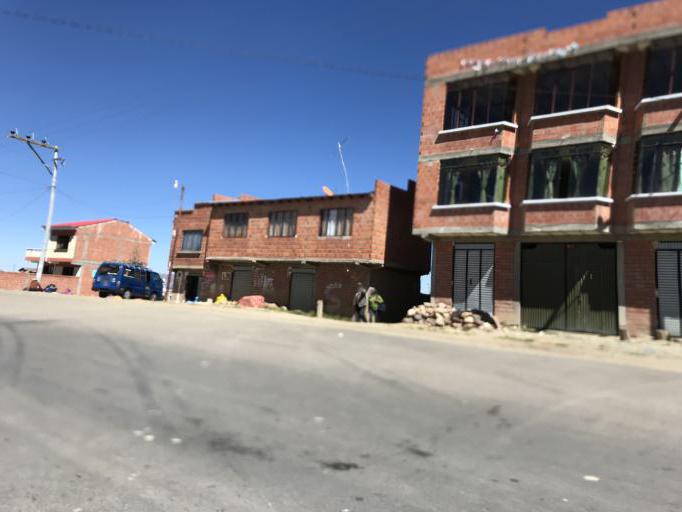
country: BO
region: La Paz
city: Huatajata
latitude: -16.2047
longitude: -68.7074
